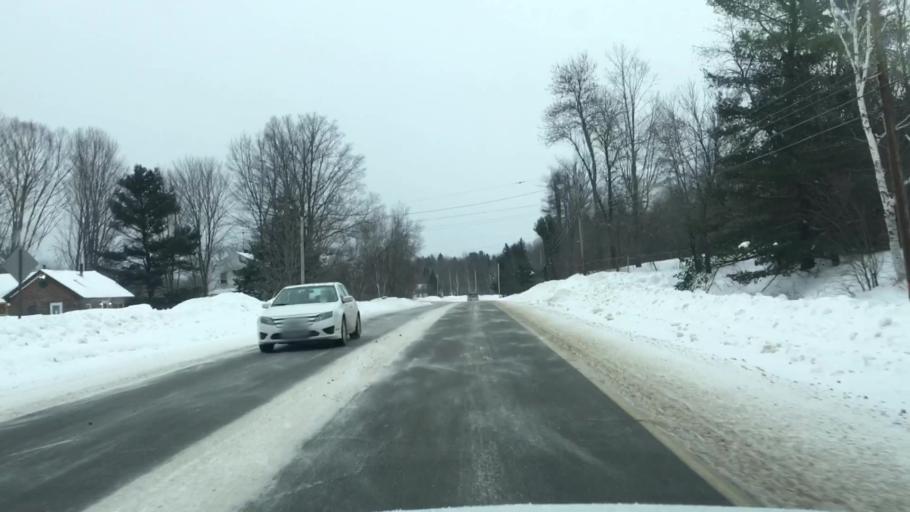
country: US
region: Maine
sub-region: Penobscot County
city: Lincoln
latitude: 45.4027
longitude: -68.4894
